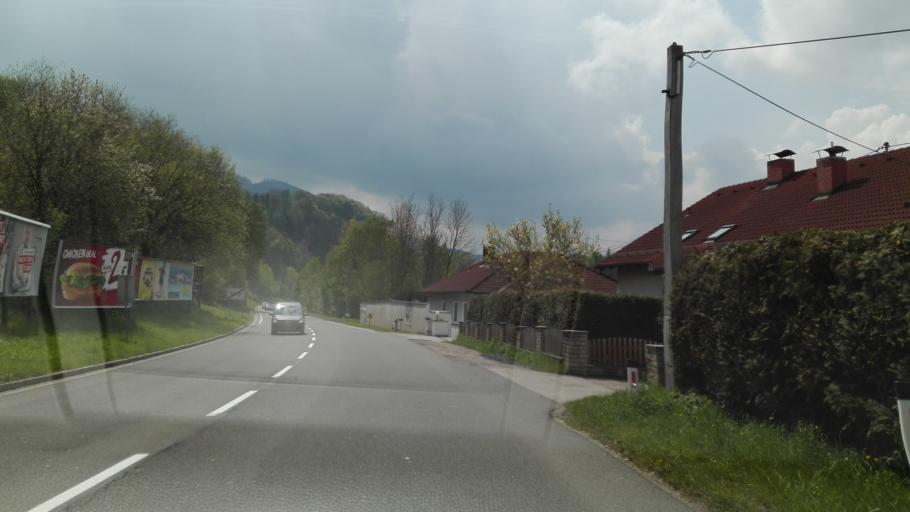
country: AT
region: Upper Austria
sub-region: Politischer Bezirk Steyr-Land
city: Sankt Ulrich bei Steyr
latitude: 48.0246
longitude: 14.4176
